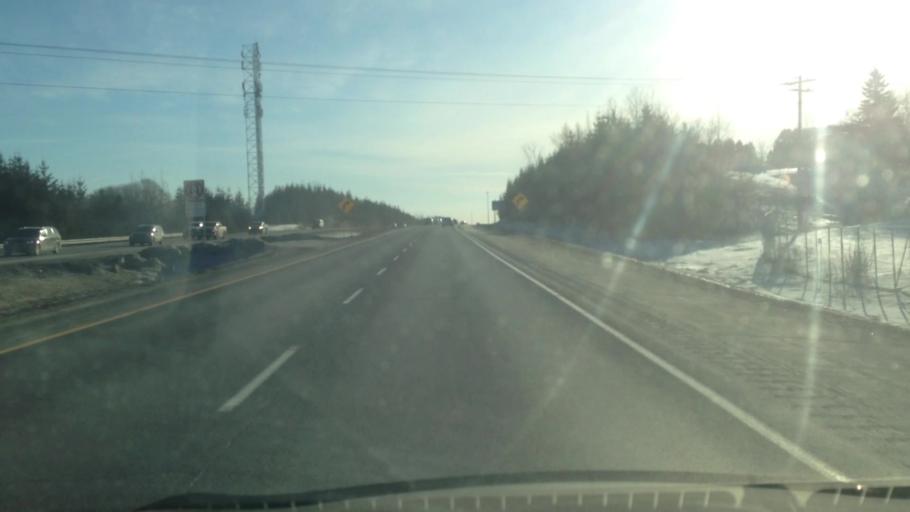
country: CA
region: Quebec
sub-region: Laurentides
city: Saint-Jerome
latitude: 45.8096
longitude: -74.0428
